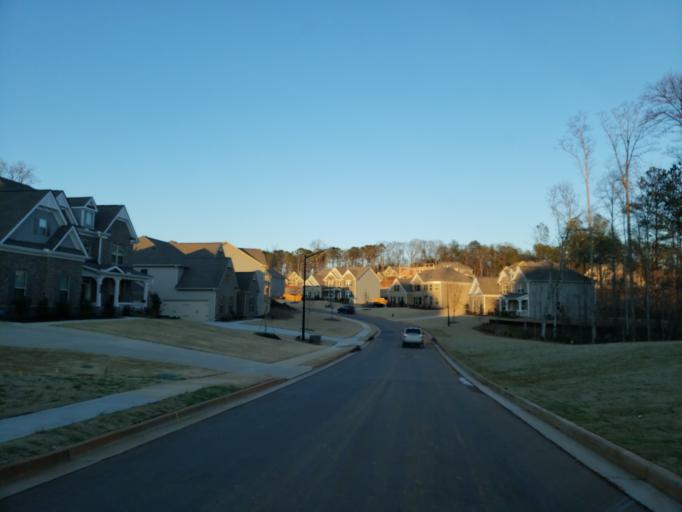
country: US
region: Georgia
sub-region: Cherokee County
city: Woodstock
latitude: 34.1175
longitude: -84.4520
